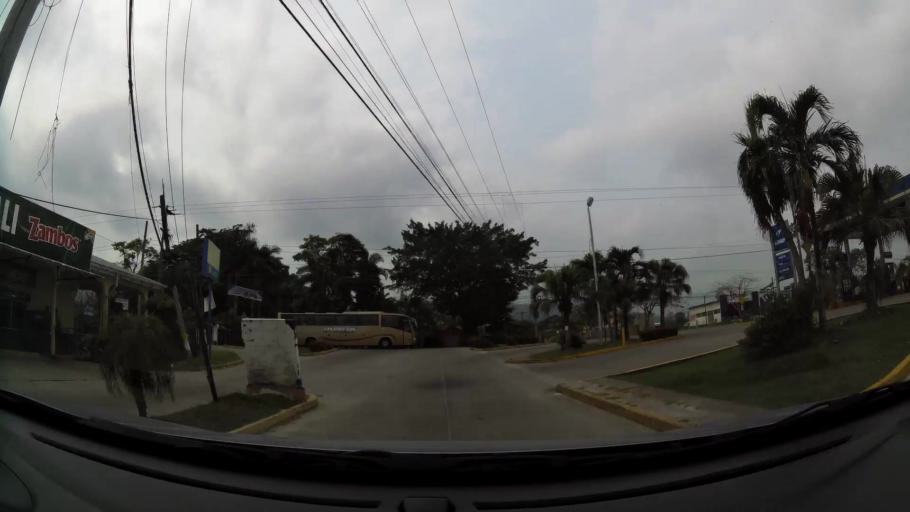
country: HN
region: Atlantida
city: Tela
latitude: 15.7626
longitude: -87.4796
